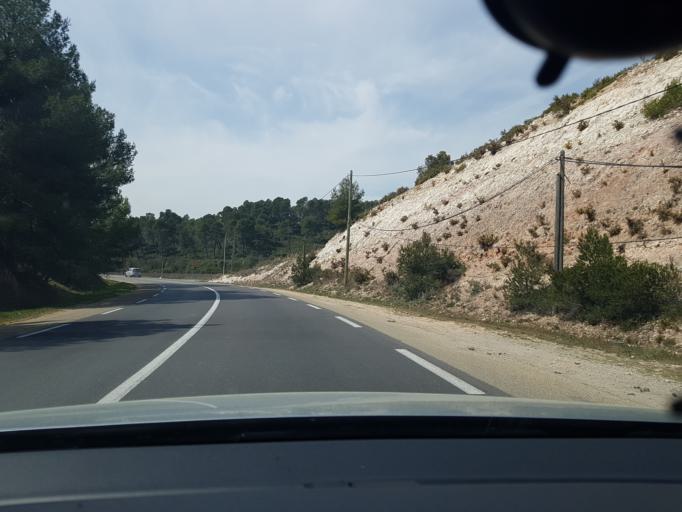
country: FR
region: Provence-Alpes-Cote d'Azur
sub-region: Departement des Bouches-du-Rhone
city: Gardanne
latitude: 43.4710
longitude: 5.4600
